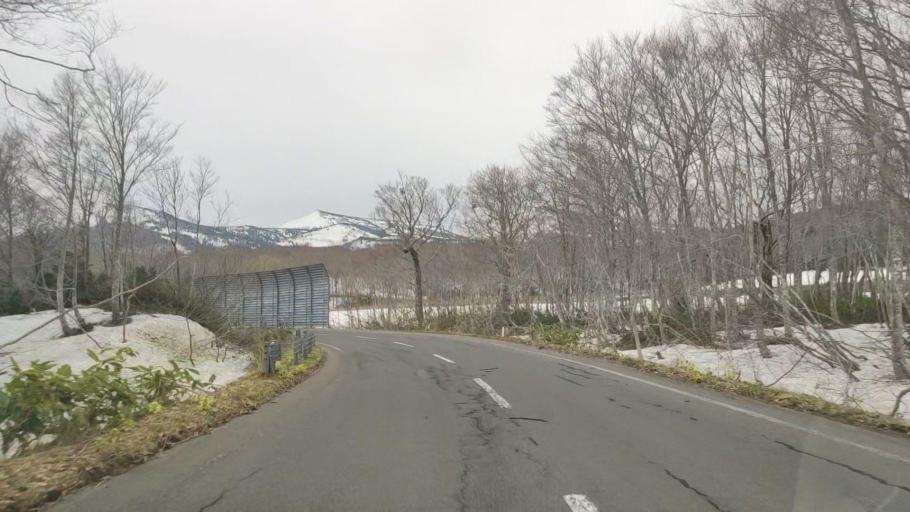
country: JP
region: Aomori
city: Aomori Shi
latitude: 40.6339
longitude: 140.9286
